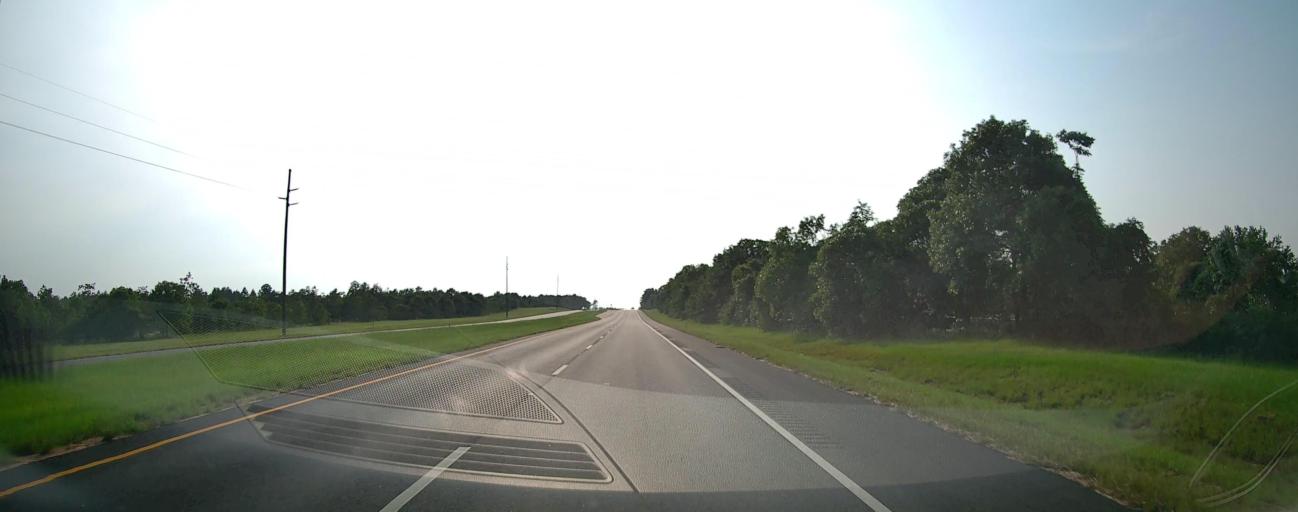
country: US
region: Georgia
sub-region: Taylor County
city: Butler
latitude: 32.5853
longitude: -84.3406
